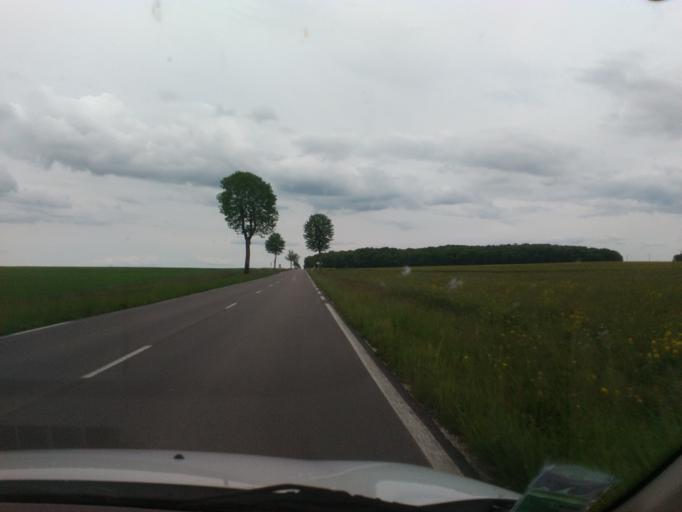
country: FR
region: Champagne-Ardenne
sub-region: Departement de l'Aube
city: Vendeuvre-sur-Barse
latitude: 48.2501
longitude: 4.5621
